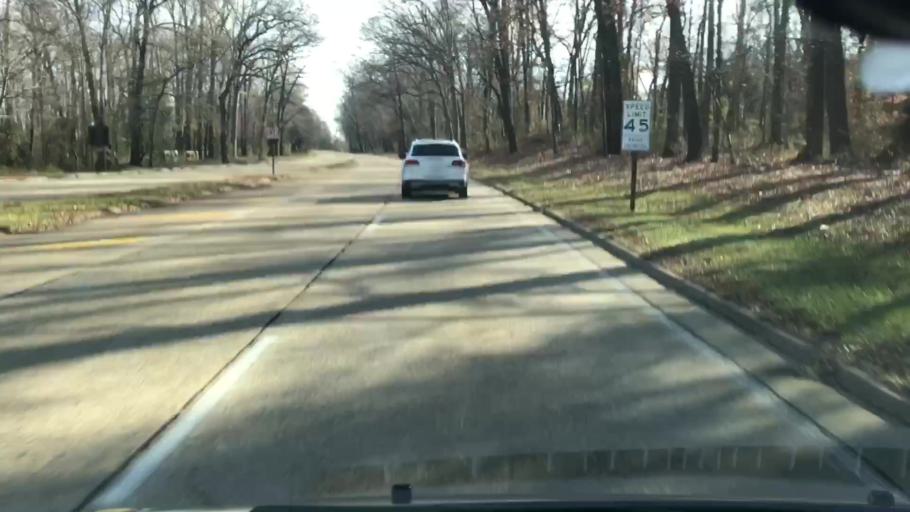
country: US
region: Virginia
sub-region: Fairfax County
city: Belle Haven
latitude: 38.7648
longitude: -77.0531
